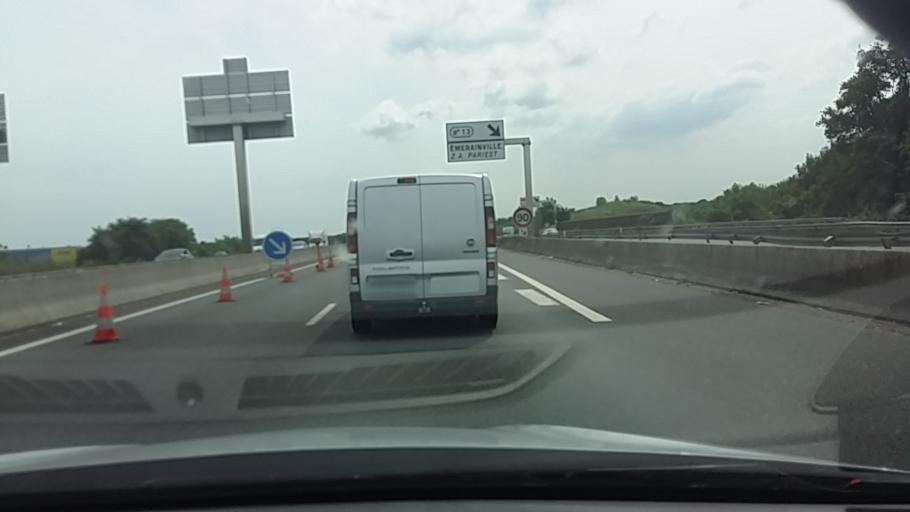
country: FR
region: Ile-de-France
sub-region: Departement de Seine-et-Marne
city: Emerainville
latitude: 48.8267
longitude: 2.6169
